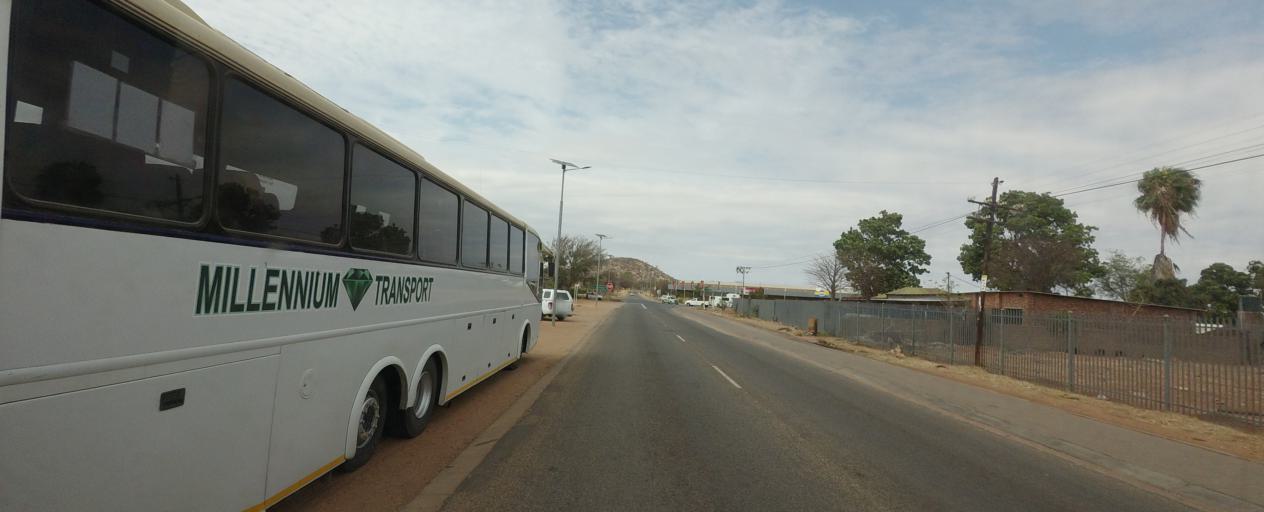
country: BW
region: Central
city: Mathathane
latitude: -22.6797
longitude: 29.1081
